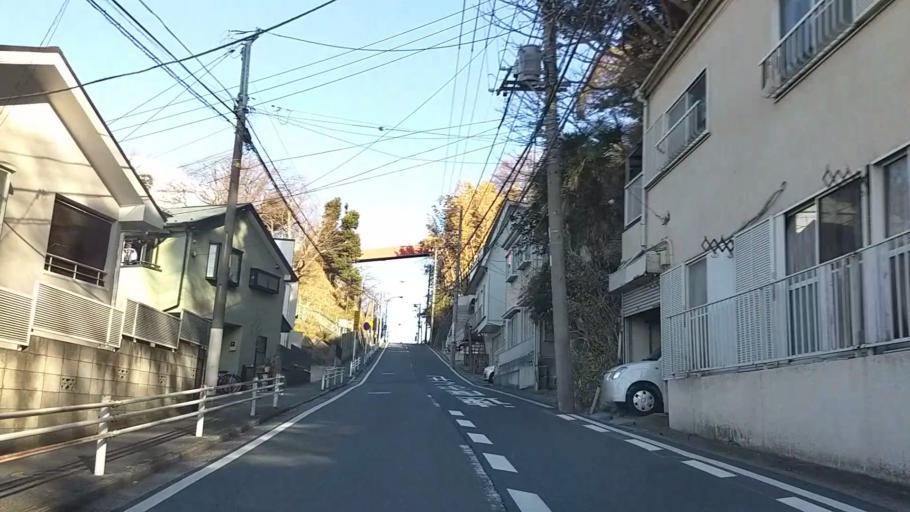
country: JP
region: Kanagawa
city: Yokohama
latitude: 35.4200
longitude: 139.6130
